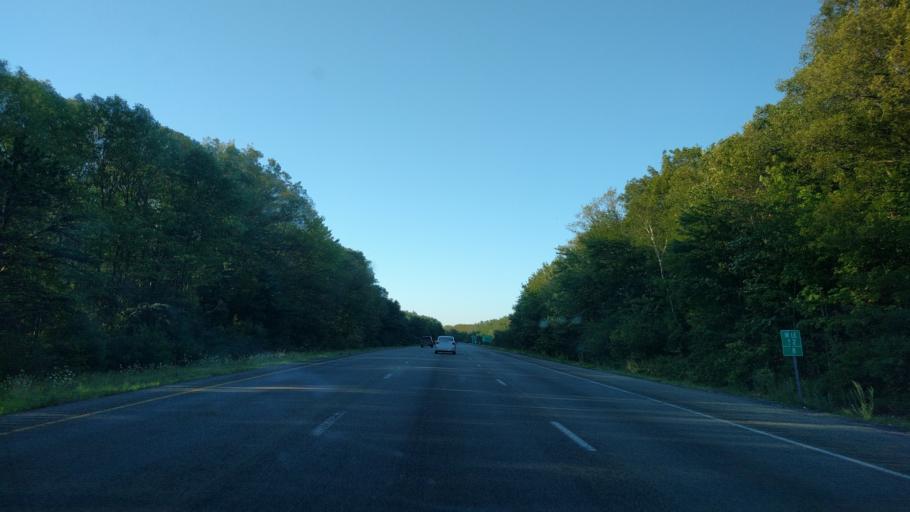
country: US
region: Massachusetts
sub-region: Middlesex County
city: Hopkinton
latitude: 42.1960
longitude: -71.5380
